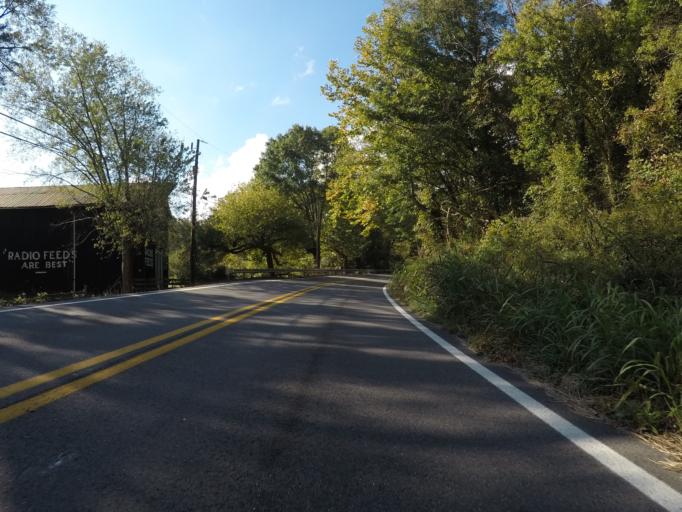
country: US
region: Ohio
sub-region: Lawrence County
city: Burlington
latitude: 38.3742
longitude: -82.5306
